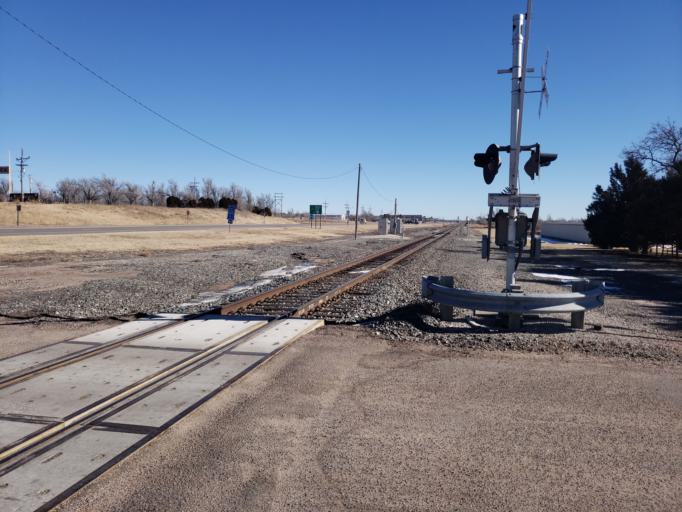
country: US
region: Kansas
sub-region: Ford County
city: Dodge City
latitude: 37.7550
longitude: -100.0697
